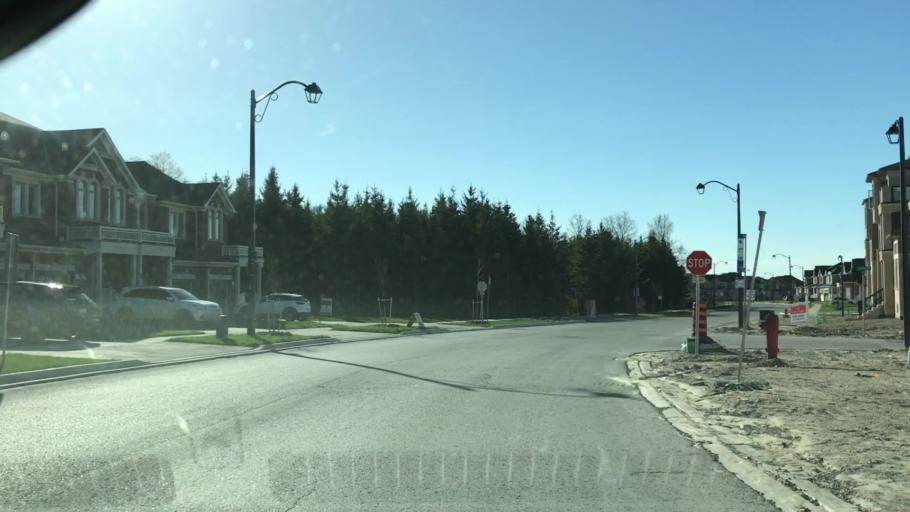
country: CA
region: Ontario
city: Newmarket
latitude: 44.0190
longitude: -79.4252
